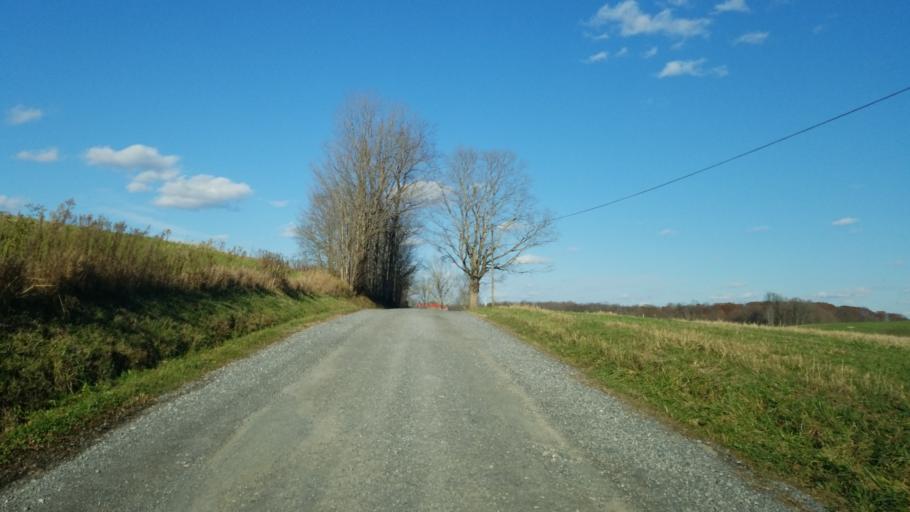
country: US
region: Pennsylvania
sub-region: Clearfield County
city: Treasure Lake
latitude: 41.1566
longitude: -78.6601
